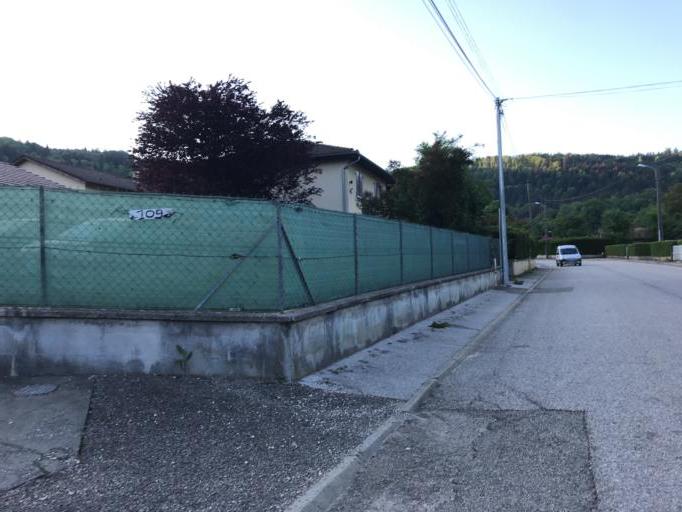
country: FR
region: Rhone-Alpes
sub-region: Departement de l'Ain
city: Oyonnax
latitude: 46.2396
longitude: 5.6678
